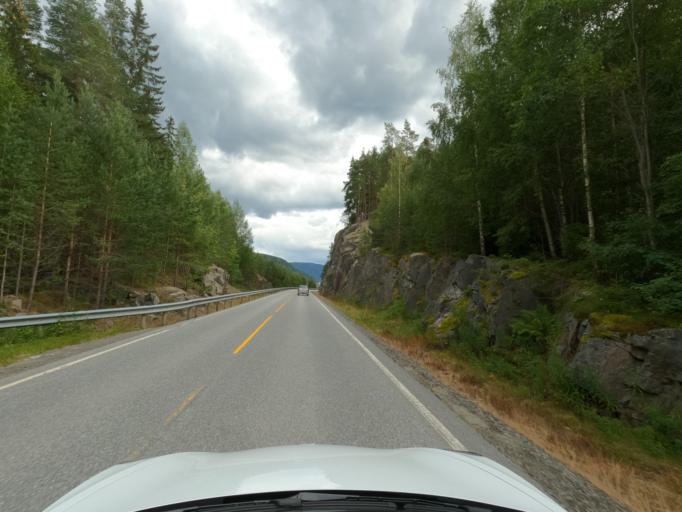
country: NO
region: Telemark
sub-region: Hjartdal
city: Sauland
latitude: 59.8683
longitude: 8.9305
